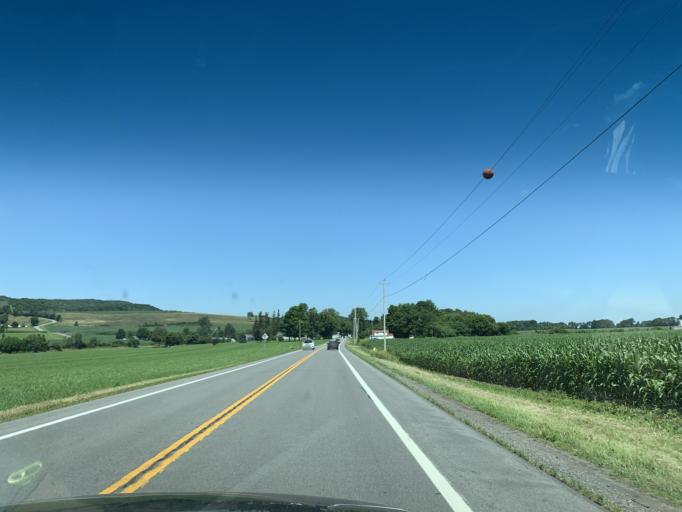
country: US
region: New York
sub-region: Oneida County
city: Chadwicks
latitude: 42.9186
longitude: -75.2441
